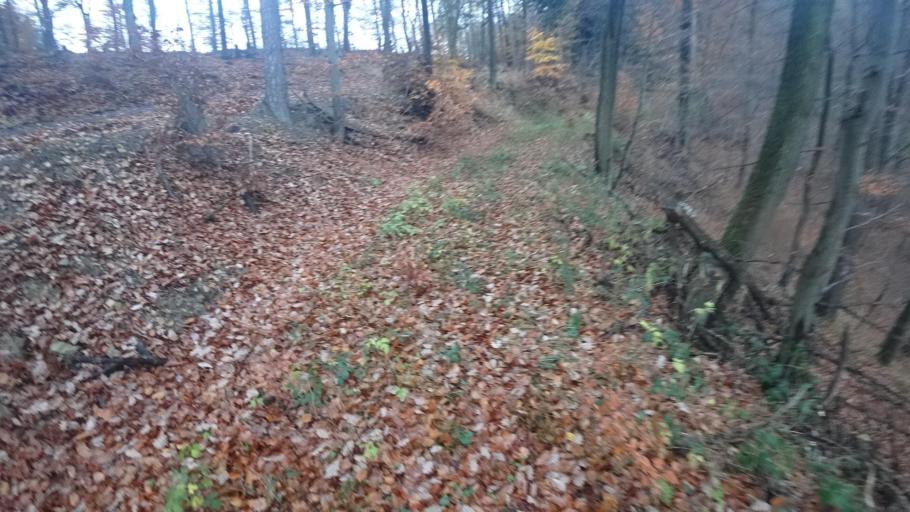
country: DE
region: Rheinland-Pfalz
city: Rech
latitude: 50.4992
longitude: 7.0530
